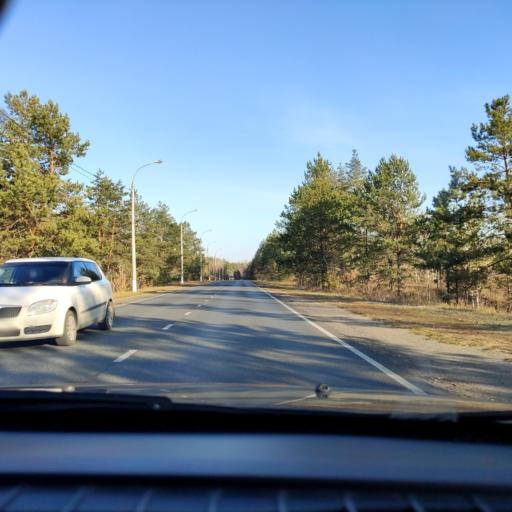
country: RU
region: Samara
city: Tol'yatti
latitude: 53.4771
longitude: 49.4295
